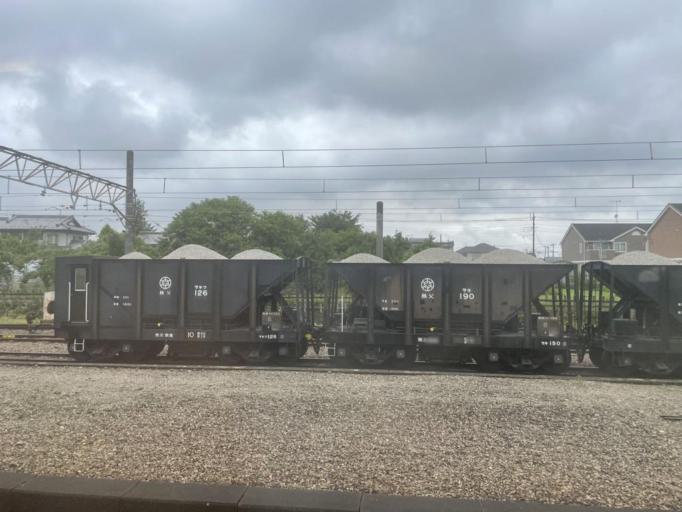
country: JP
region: Saitama
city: Fukayacho
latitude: 36.1423
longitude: 139.2820
